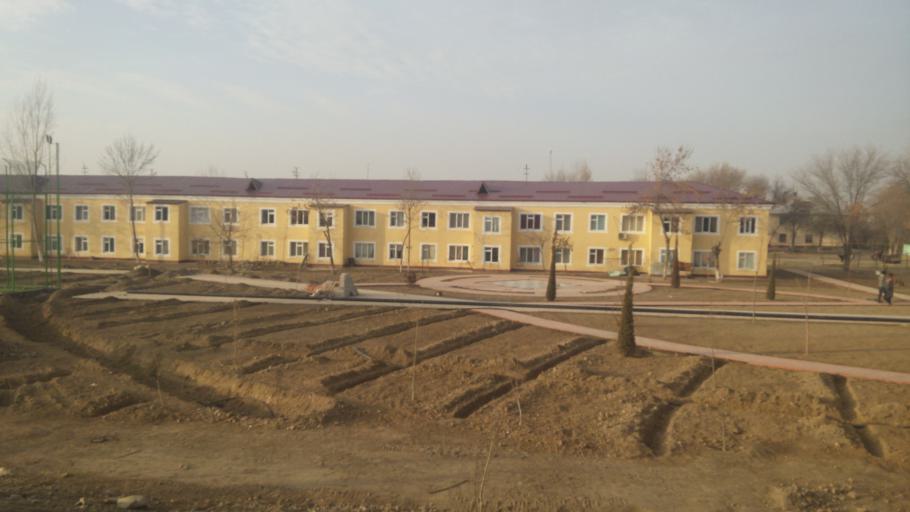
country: UZ
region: Sirdaryo
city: Guliston
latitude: 40.5097
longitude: 68.7779
